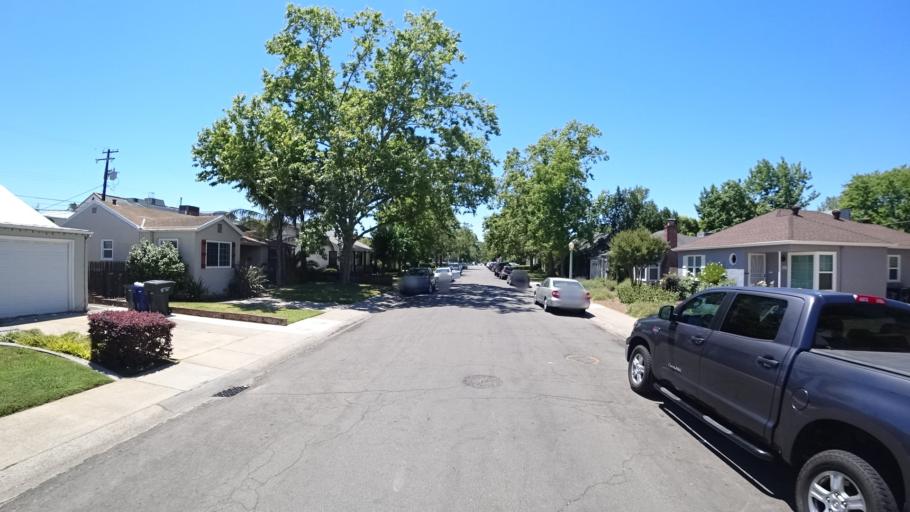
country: US
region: California
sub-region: Sacramento County
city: Sacramento
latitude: 38.5688
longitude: -121.4348
